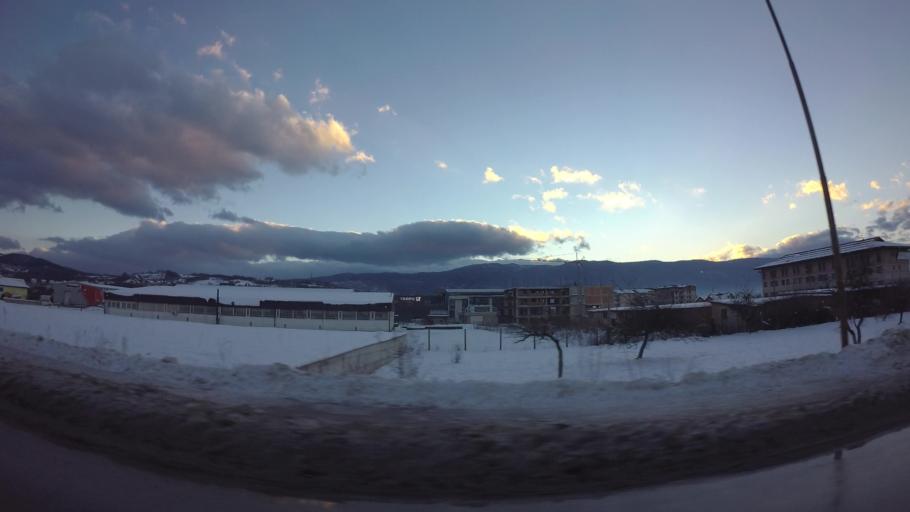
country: BA
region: Federation of Bosnia and Herzegovina
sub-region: Kanton Sarajevo
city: Sarajevo
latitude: 43.8186
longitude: 18.3576
